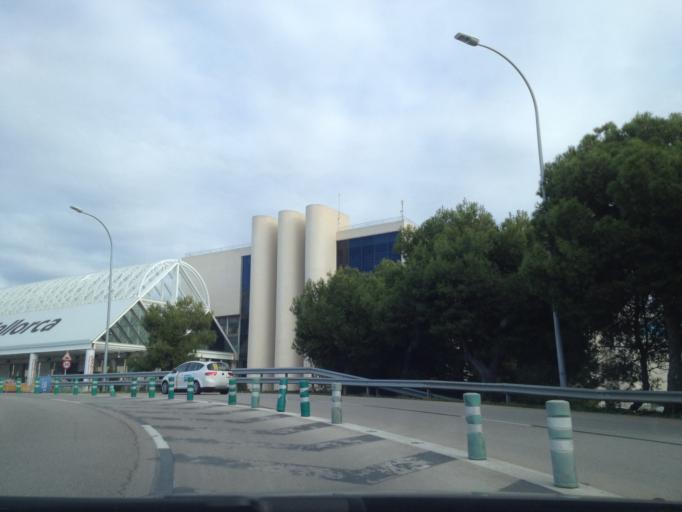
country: ES
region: Balearic Islands
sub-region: Illes Balears
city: s'Arenal
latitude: 39.5458
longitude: 2.7313
